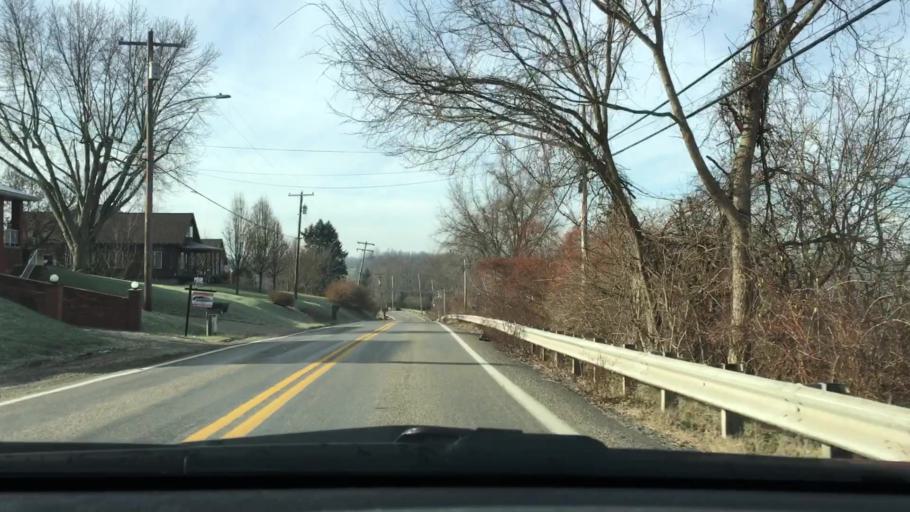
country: US
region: Pennsylvania
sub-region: Allegheny County
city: Jefferson Hills
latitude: 40.2799
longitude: -79.9294
